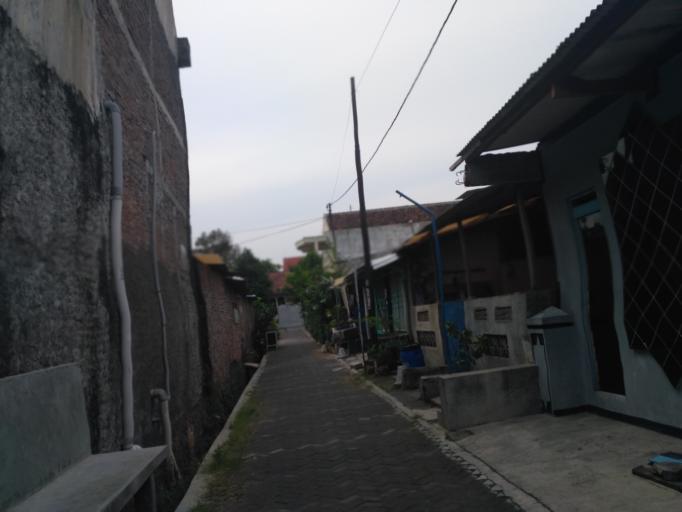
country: ID
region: Central Java
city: Ungaran
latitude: -7.0706
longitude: 110.4279
